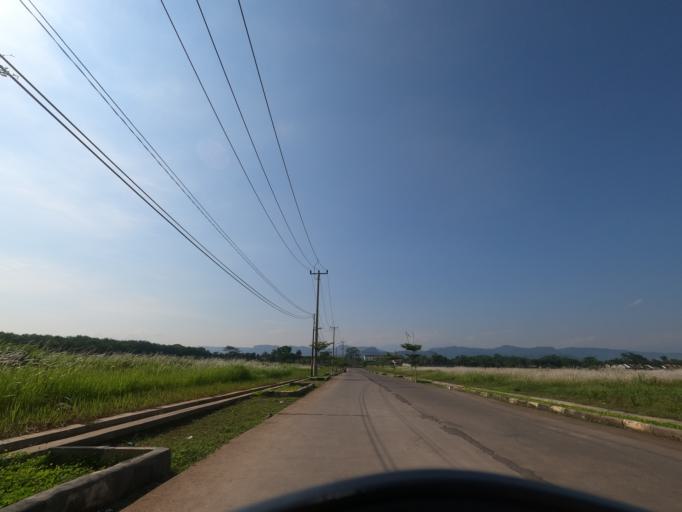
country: ID
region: West Java
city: Pamanukan
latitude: -6.5746
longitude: 107.7912
